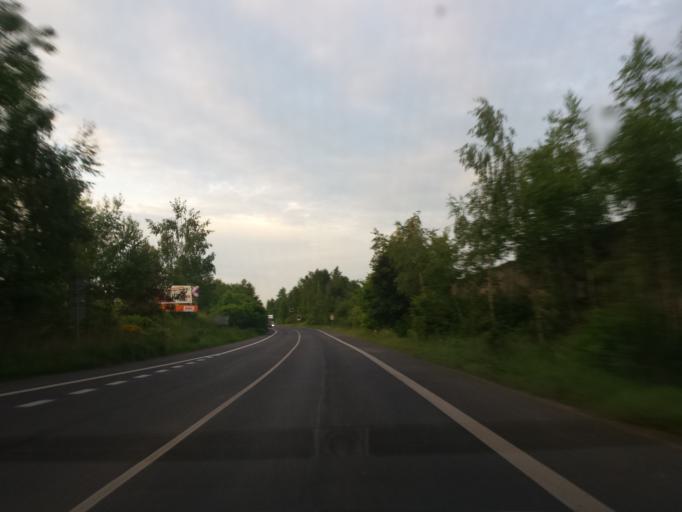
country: CZ
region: Liberecky
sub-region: Okres Ceska Lipa
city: Ceska Lipa
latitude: 50.6737
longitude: 14.5420
